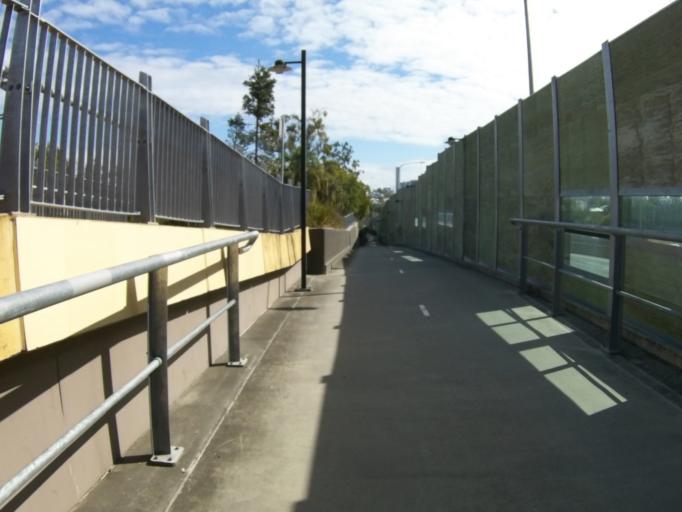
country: AU
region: Queensland
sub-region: Brisbane
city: Woolloongabba
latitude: -27.4961
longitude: 153.0376
